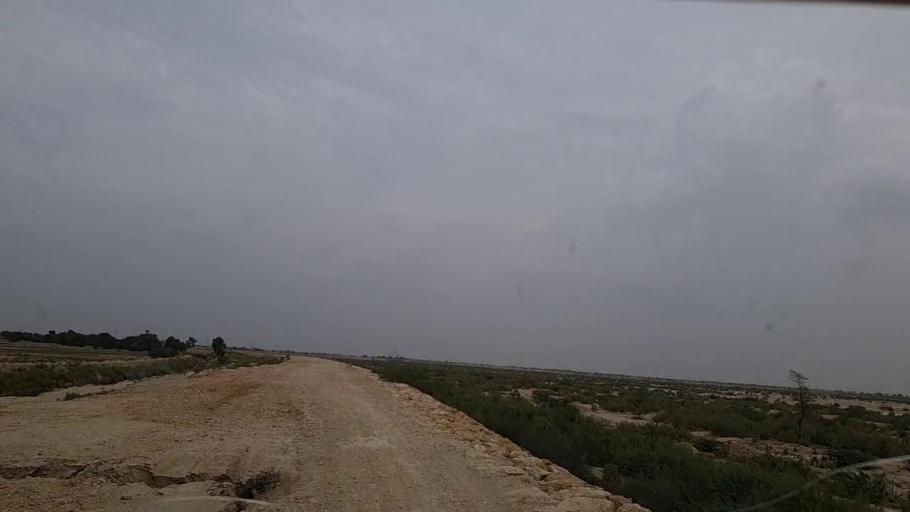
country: PK
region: Sindh
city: Johi
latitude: 26.7088
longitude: 67.5869
